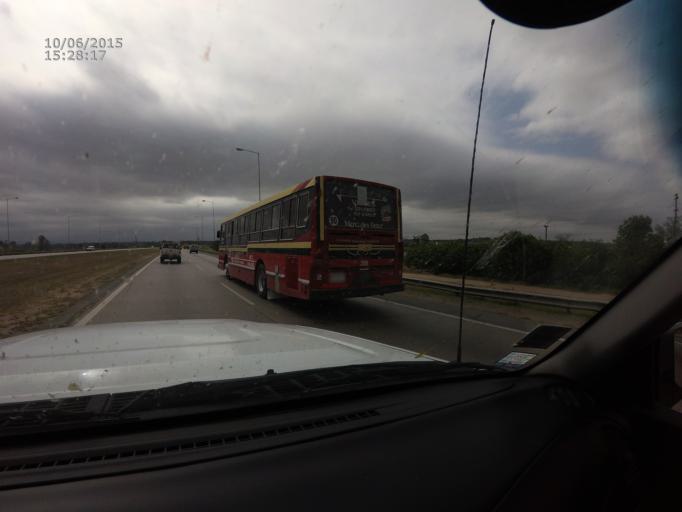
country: AR
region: Cordoba
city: Malvinas Argentinas
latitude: -31.4122
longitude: -64.1190
